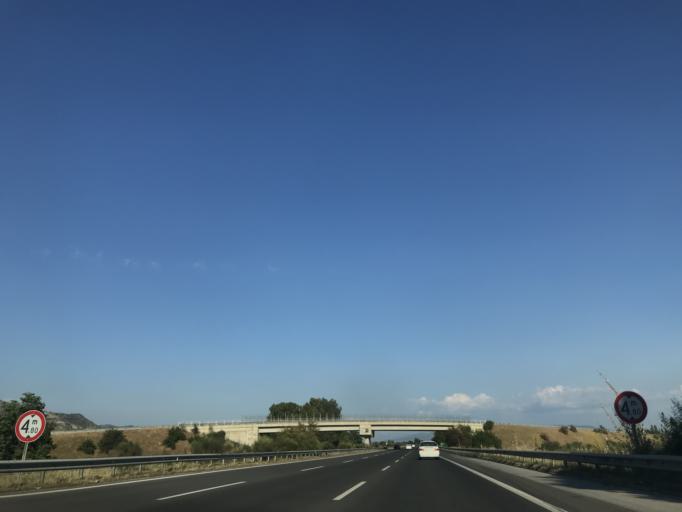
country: TR
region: Aydin
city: Incirliova
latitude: 37.8712
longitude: 27.7095
